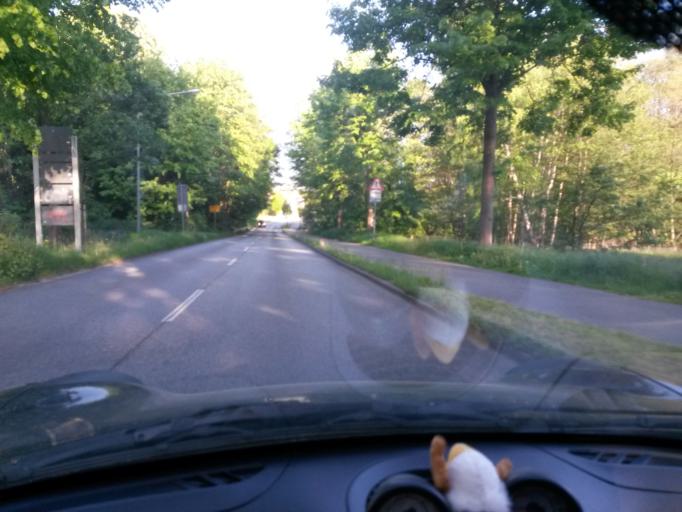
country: DE
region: Schleswig-Holstein
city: Gross Gronau
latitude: 53.8461
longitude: 10.7504
